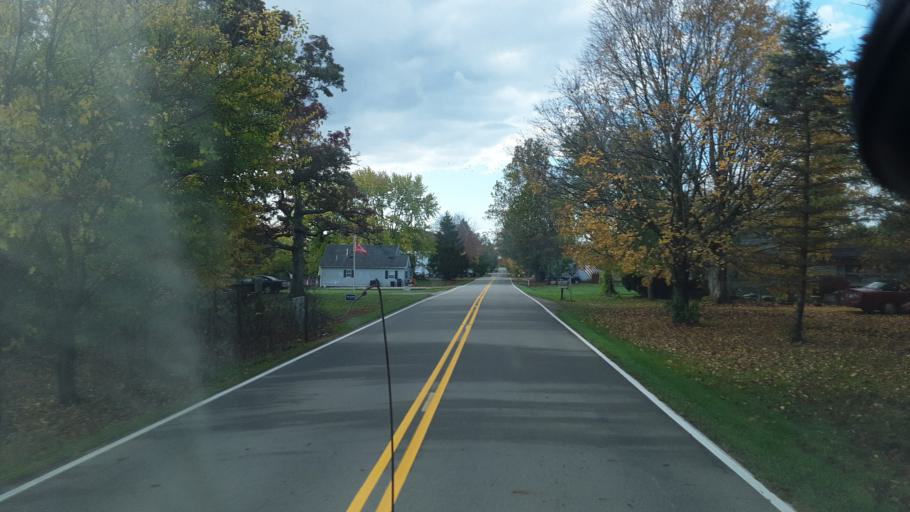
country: US
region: Ohio
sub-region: Highland County
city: Greenfield
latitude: 39.3995
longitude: -83.4622
